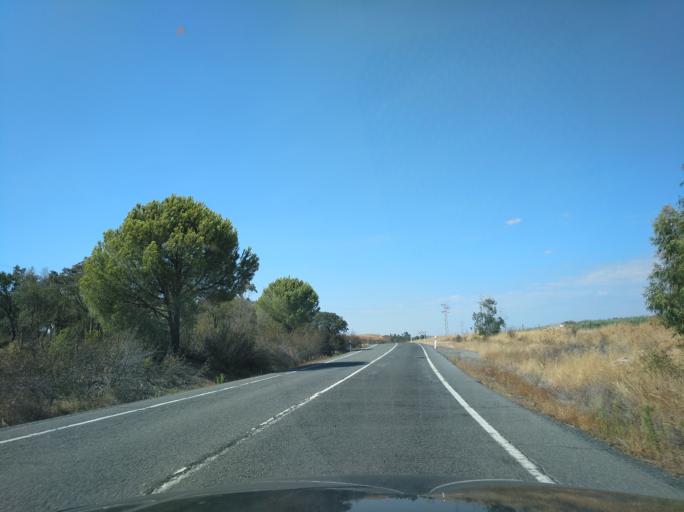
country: ES
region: Andalusia
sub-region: Provincia de Huelva
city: San Bartolome de la Torre
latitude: 37.4874
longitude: -7.1321
